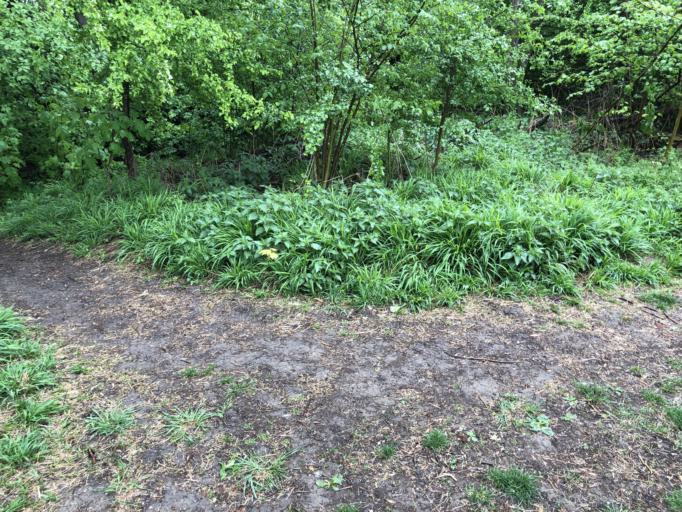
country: DE
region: Baden-Wuerttemberg
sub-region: Regierungsbezirk Stuttgart
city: Neuhausen auf den Fildern
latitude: 48.6893
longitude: 9.2993
